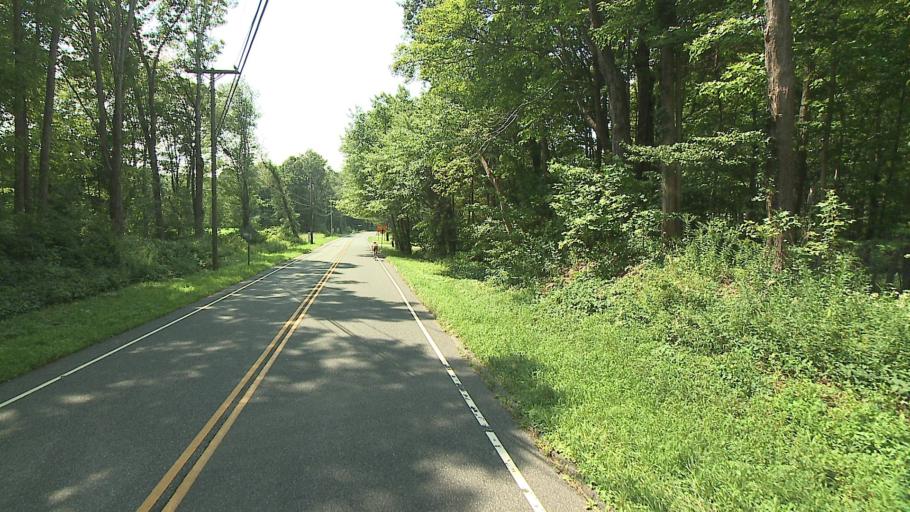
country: US
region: Connecticut
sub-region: Litchfield County
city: New Preston
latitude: 41.6574
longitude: -73.2793
